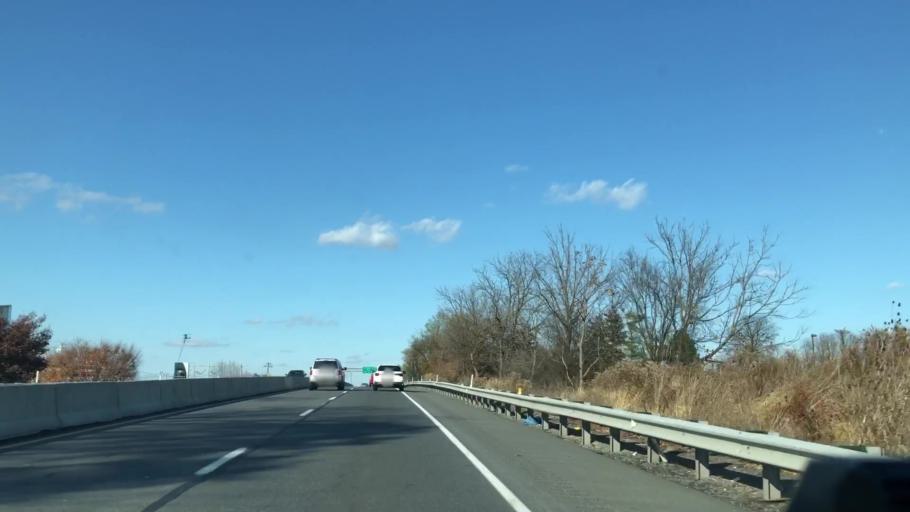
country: US
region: Pennsylvania
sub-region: Lehigh County
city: Wescosville
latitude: 40.5855
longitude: -75.5533
